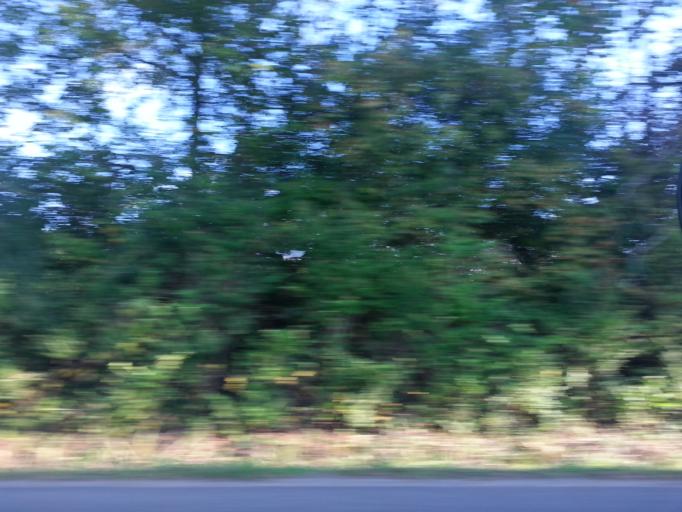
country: US
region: Tennessee
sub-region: Blount County
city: Eagleton Village
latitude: 35.7906
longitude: -83.9178
